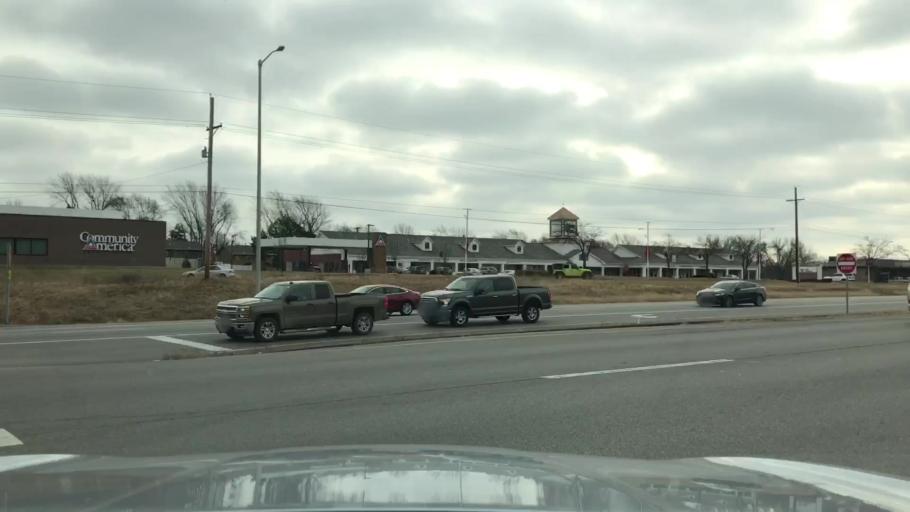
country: US
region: Missouri
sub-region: Jackson County
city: Lees Summit
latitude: 38.9269
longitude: -94.3590
